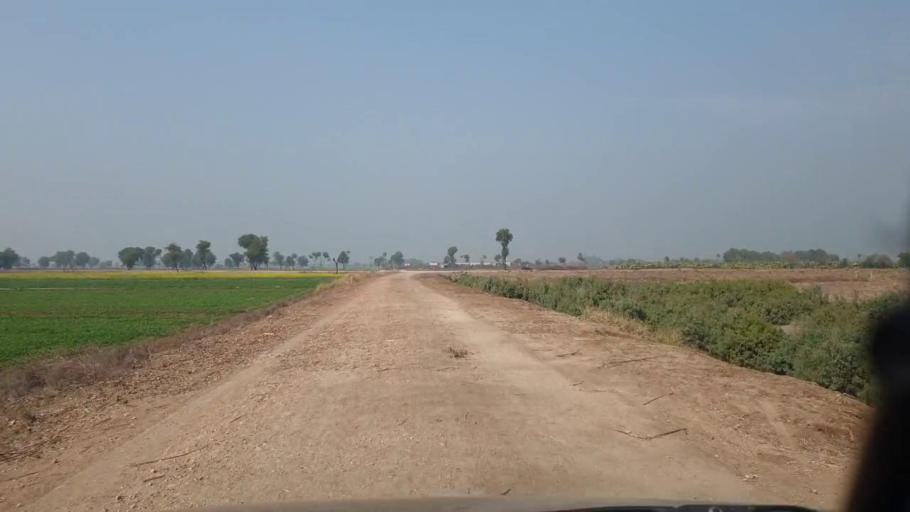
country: PK
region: Sindh
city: Shahdadpur
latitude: 26.0360
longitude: 68.5031
